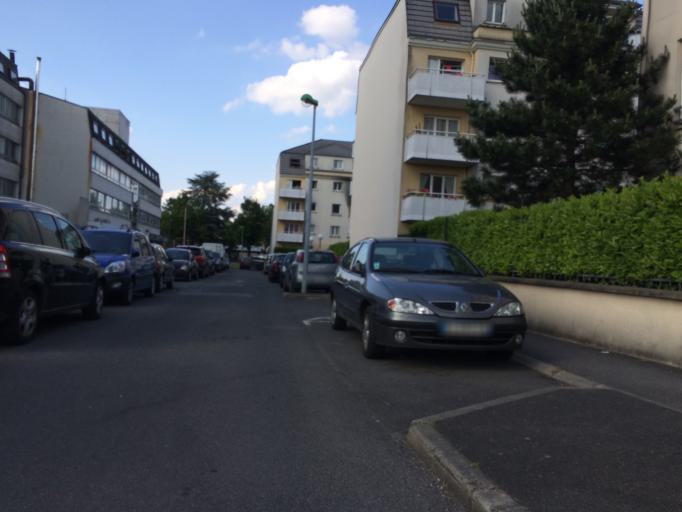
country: FR
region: Ile-de-France
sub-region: Departement de l'Essonne
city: Grigny
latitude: 48.6510
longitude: 2.3995
